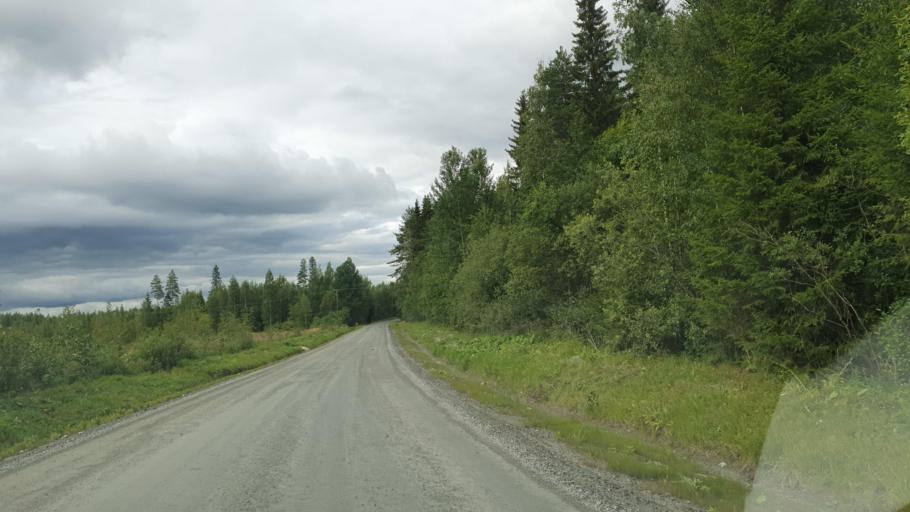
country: FI
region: Northern Savo
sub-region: Ylae-Savo
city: Iisalmi
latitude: 63.5271
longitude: 27.0891
